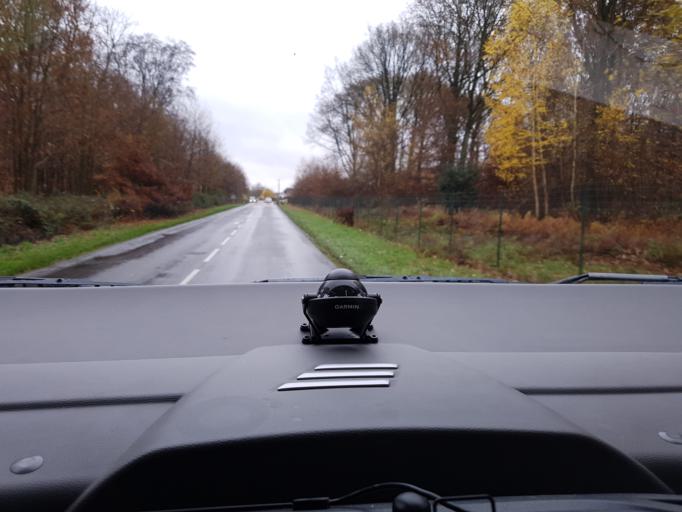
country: FR
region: Haute-Normandie
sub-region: Departement de l'Eure
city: Pont-Saint-Pierre
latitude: 49.3181
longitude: 1.2998
